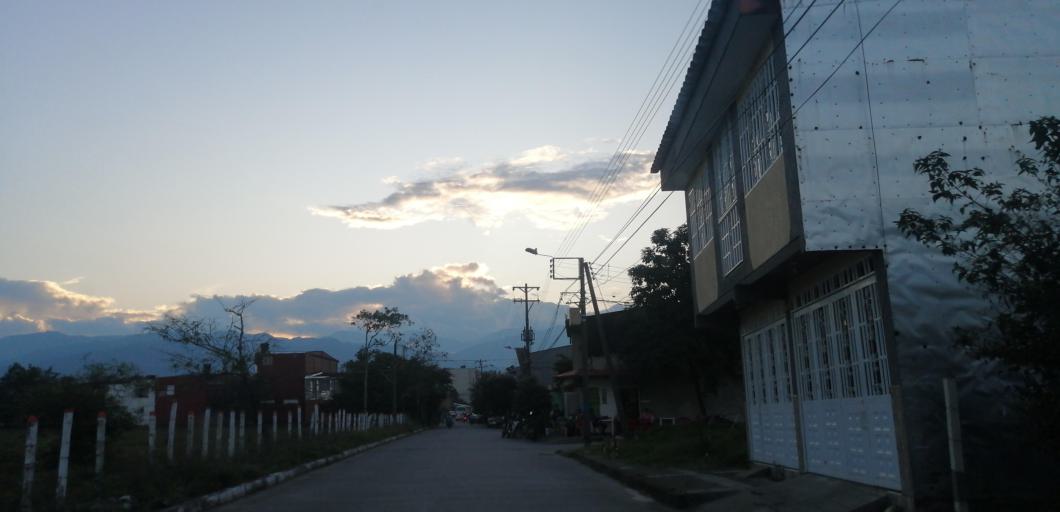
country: CO
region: Meta
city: Acacias
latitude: 3.9972
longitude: -73.7570
